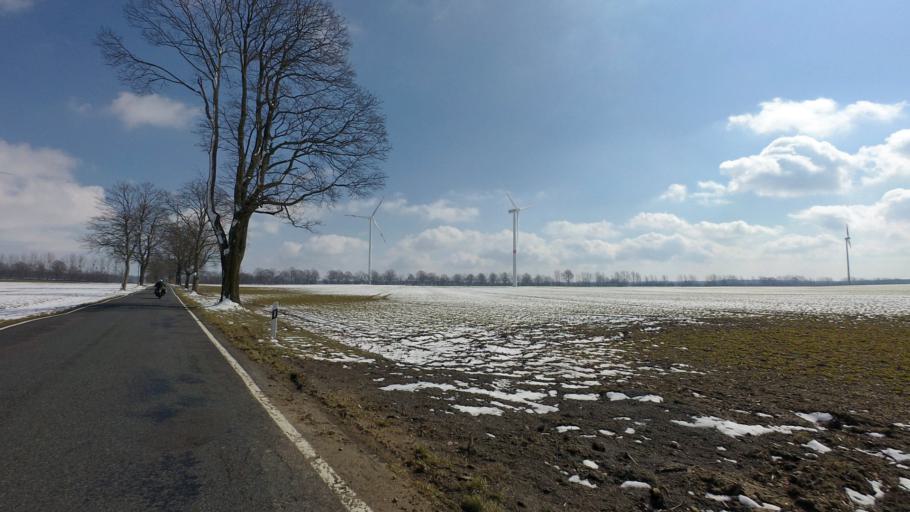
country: DE
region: Brandenburg
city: Werftpfuhl
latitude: 52.6998
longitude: 13.8296
